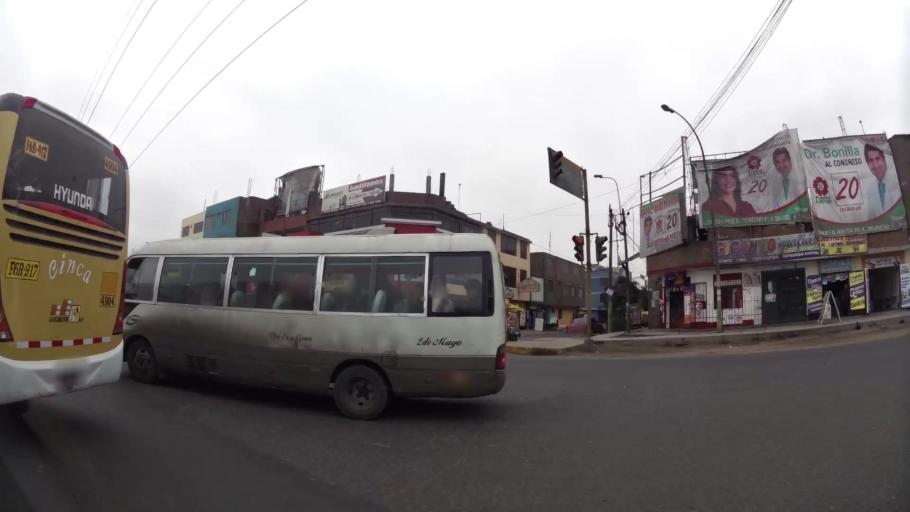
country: PE
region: Lima
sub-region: Lima
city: Vitarte
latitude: -12.0434
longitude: -76.9701
